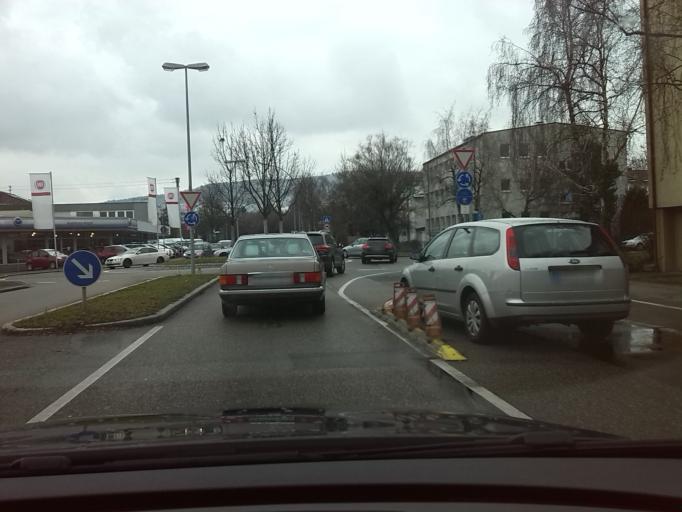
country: DE
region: Baden-Wuerttemberg
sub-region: Regierungsbezirk Stuttgart
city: Fellbach
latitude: 48.8146
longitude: 9.2840
